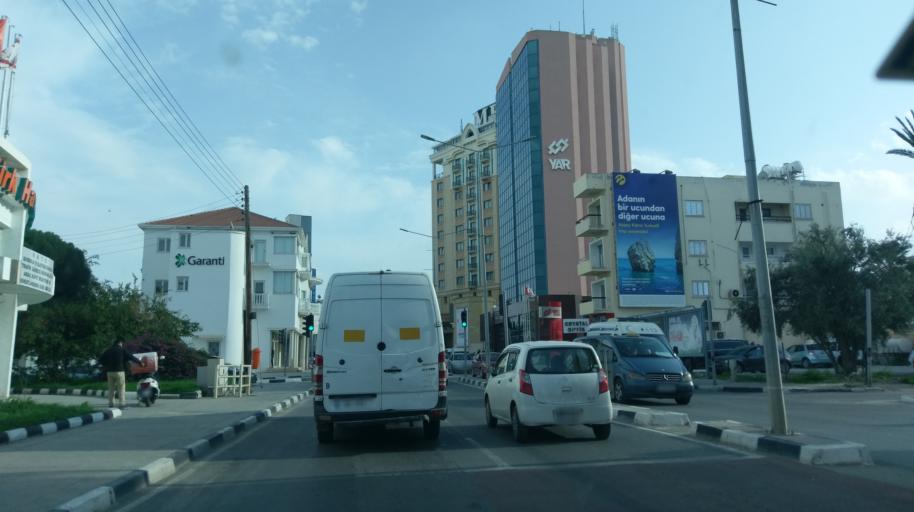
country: CY
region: Lefkosia
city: Nicosia
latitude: 35.1914
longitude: 33.3515
